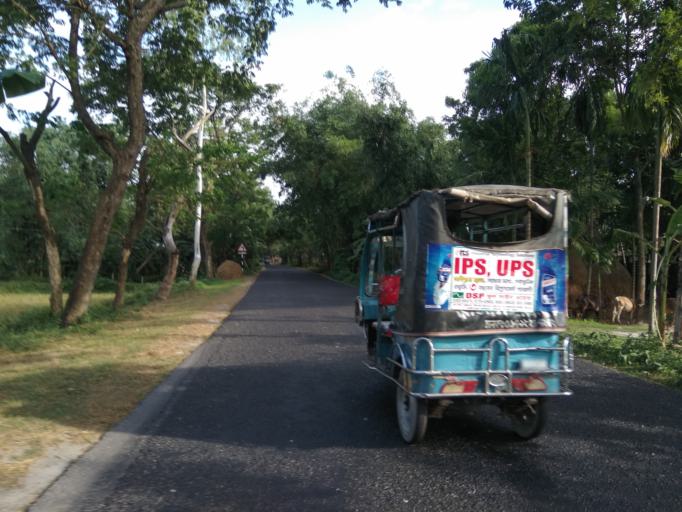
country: BD
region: Rangpur Division
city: Rangpur
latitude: 25.8389
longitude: 89.1139
